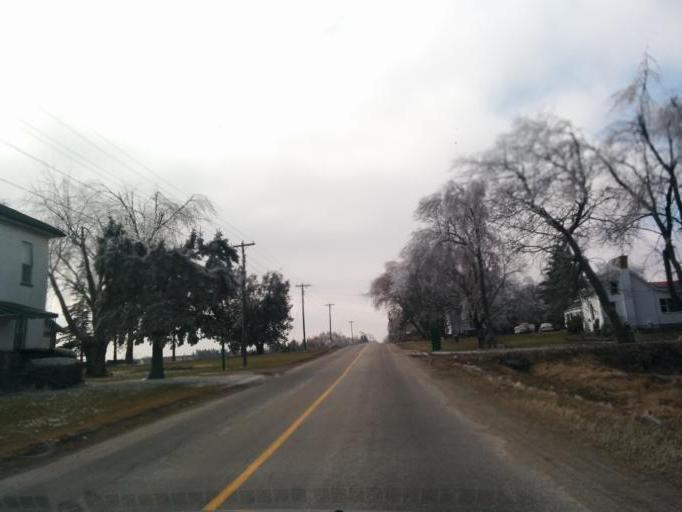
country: CA
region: Ontario
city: Waterloo
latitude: 43.6344
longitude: -80.5665
